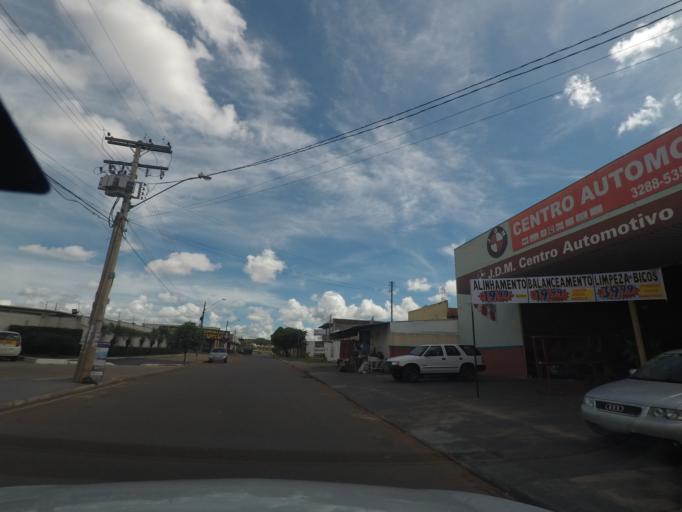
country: BR
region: Goias
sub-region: Goiania
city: Goiania
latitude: -16.7417
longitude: -49.3429
